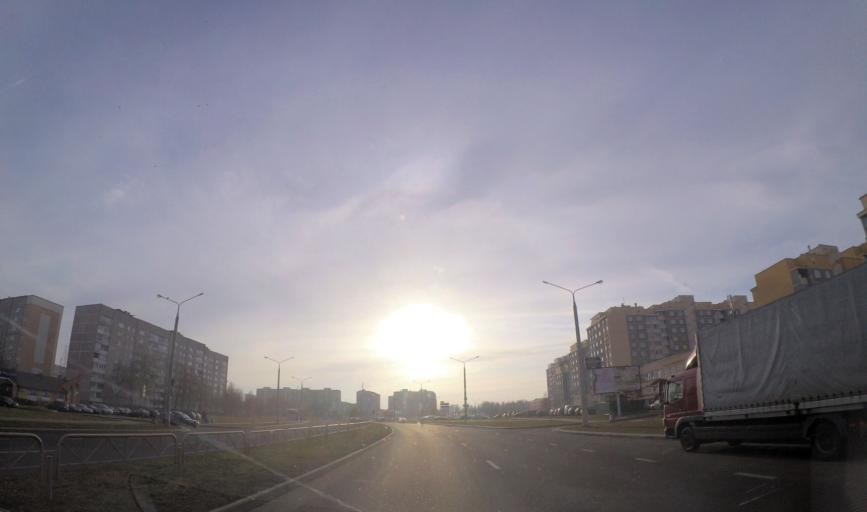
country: BY
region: Grodnenskaya
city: Hrodna
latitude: 53.6597
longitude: 23.7820
